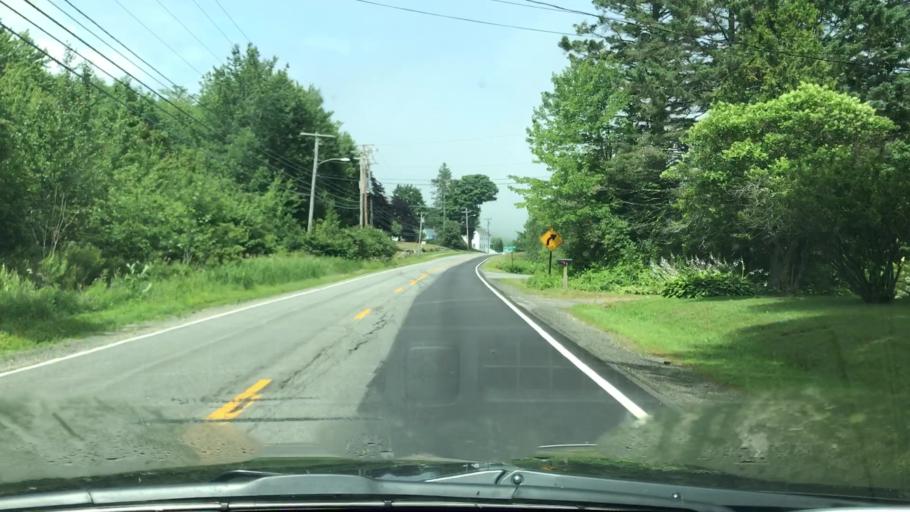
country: US
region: Maine
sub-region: Waldo County
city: Lincolnville
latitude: 44.2930
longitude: -69.0078
